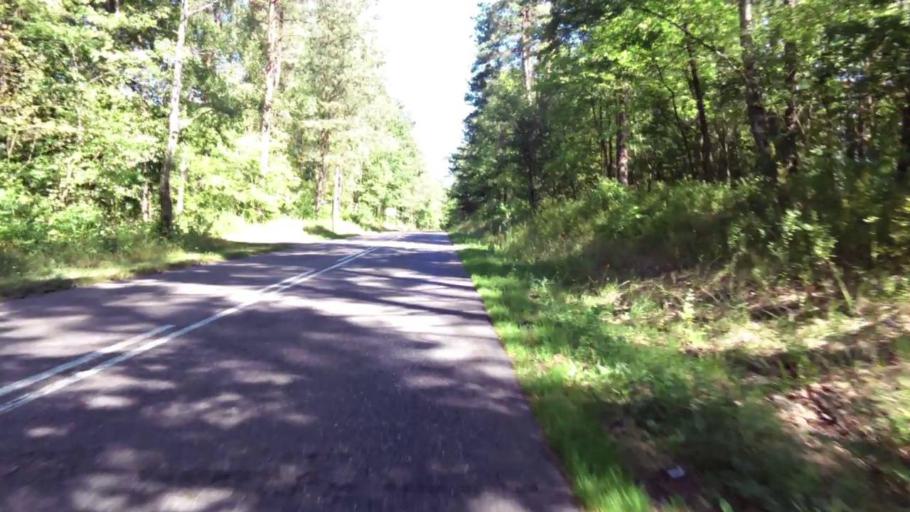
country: PL
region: West Pomeranian Voivodeship
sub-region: Powiat szczecinecki
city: Borne Sulinowo
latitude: 53.5800
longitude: 16.5690
